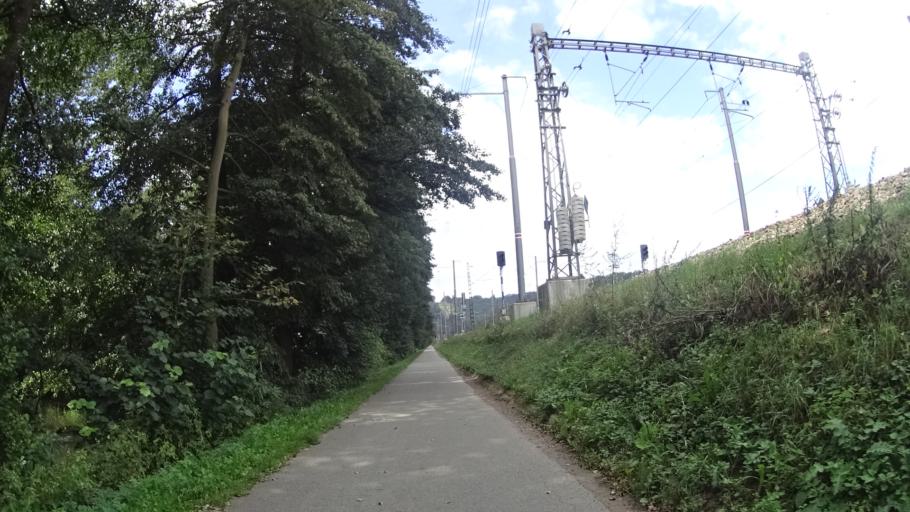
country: CZ
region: Pardubicky
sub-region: Okres Usti nad Orlici
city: Usti nad Orlici
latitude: 49.9728
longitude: 16.3595
